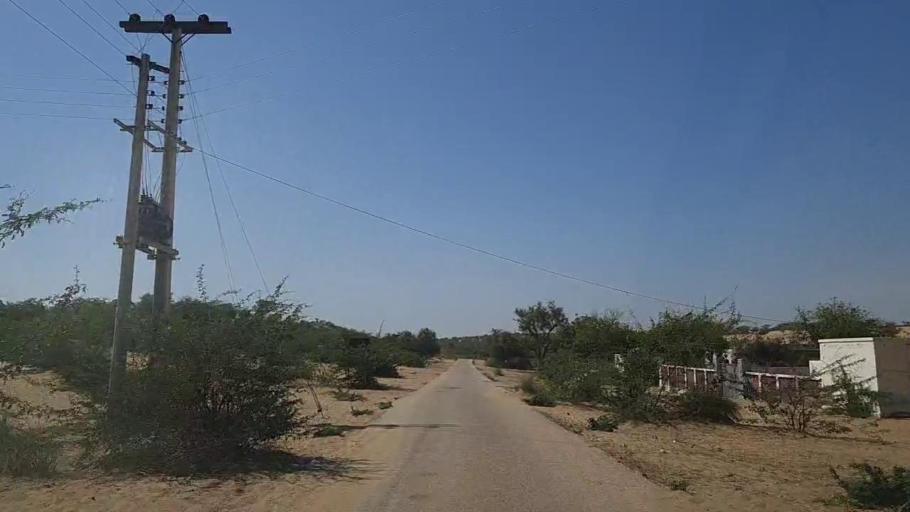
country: PK
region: Sindh
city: Mithi
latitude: 24.8242
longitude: 69.6769
